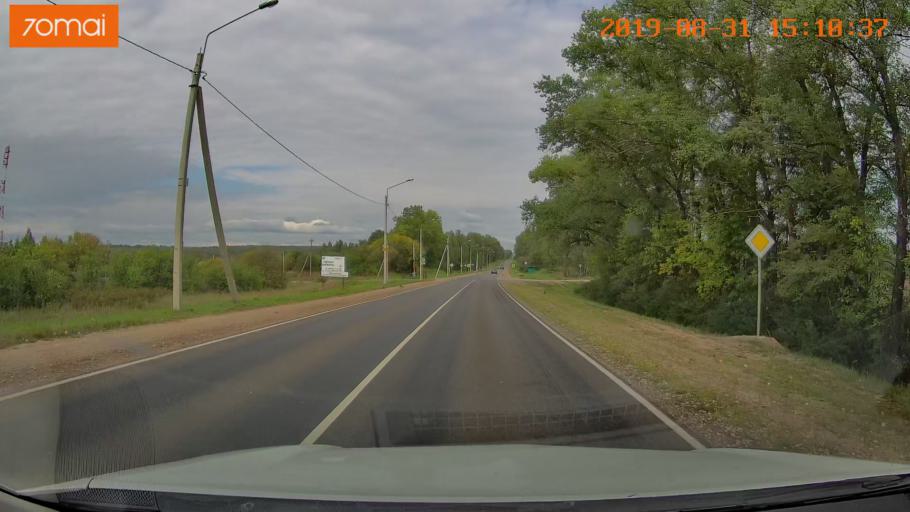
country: RU
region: Kaluga
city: Spas-Demensk
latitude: 54.4156
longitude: 34.2243
